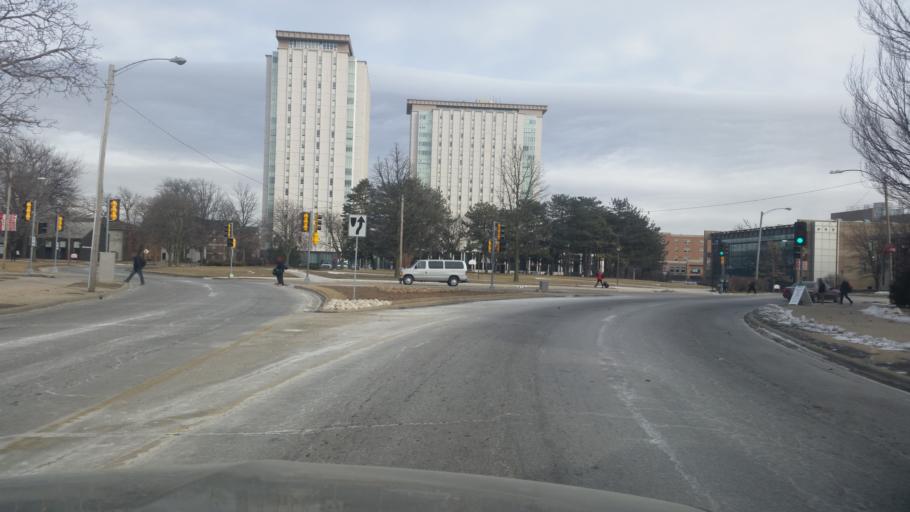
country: US
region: Illinois
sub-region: McLean County
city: Normal
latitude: 40.5108
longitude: -88.9903
